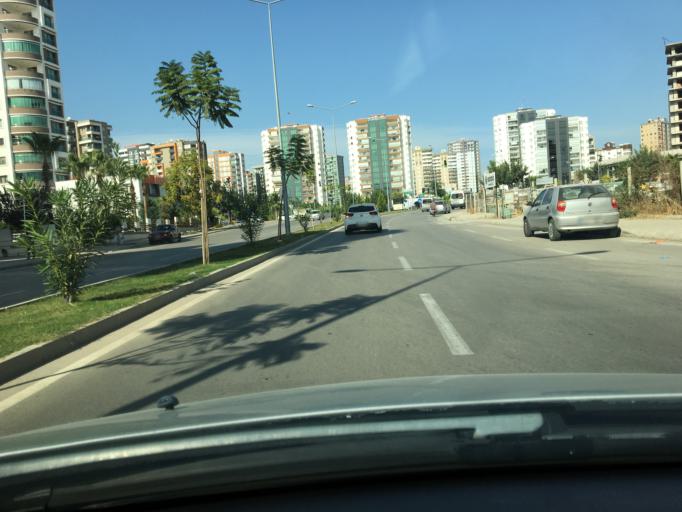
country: TR
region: Adana
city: Seyhan
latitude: 37.0212
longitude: 35.2581
